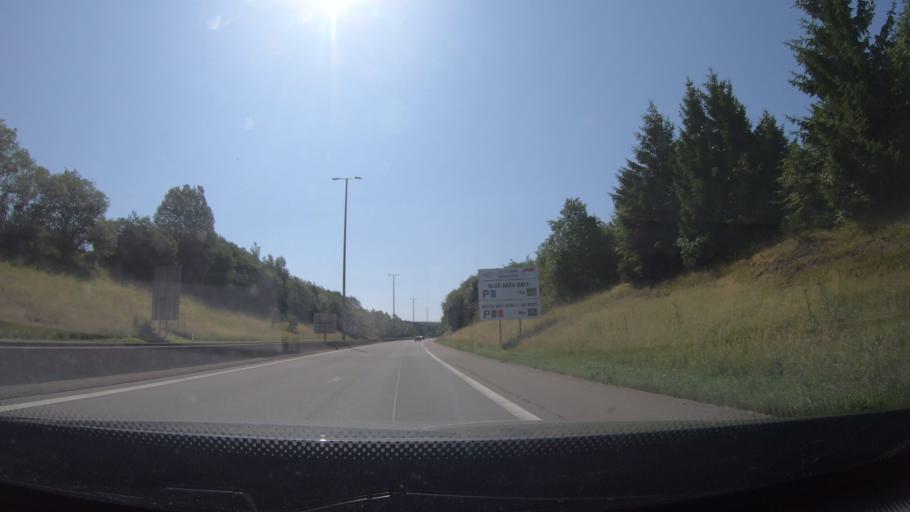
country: BE
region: Wallonia
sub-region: Province de Liege
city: Malmedy
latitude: 50.4711
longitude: 5.9838
